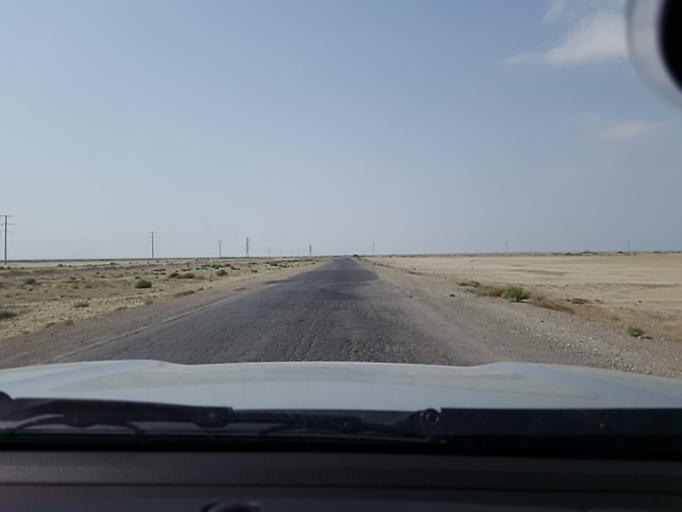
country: TM
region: Balkan
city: Gumdag
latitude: 39.0077
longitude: 54.5858
